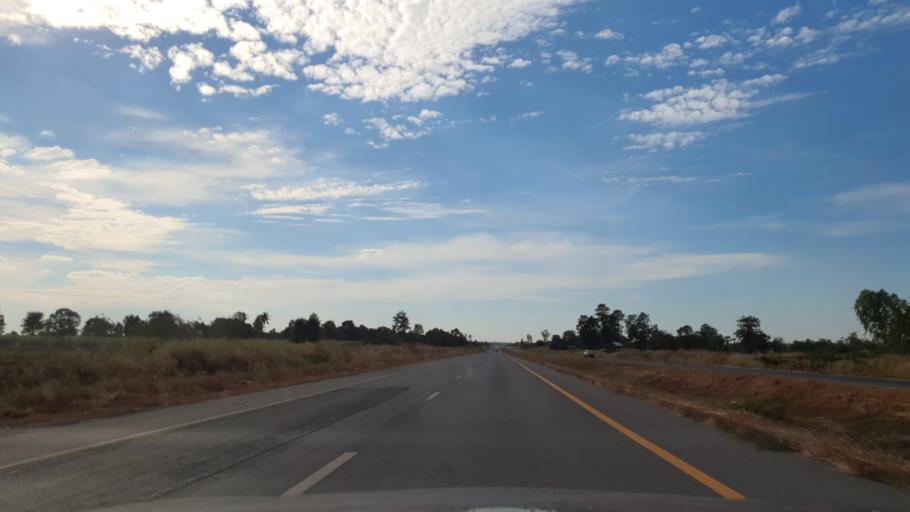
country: TH
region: Roi Et
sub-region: Amphoe Pho Chai
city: Pho Chai
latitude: 16.4133
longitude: 103.7804
